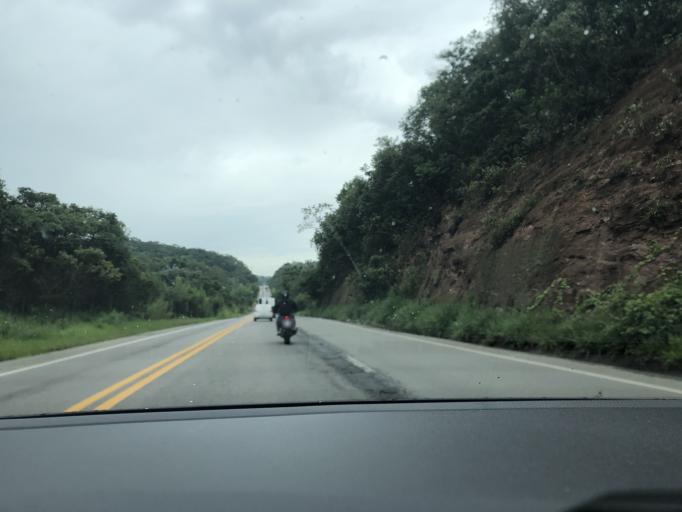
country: BR
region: Sao Paulo
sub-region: Jarinu
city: Jarinu
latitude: -23.1530
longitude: -46.7458
